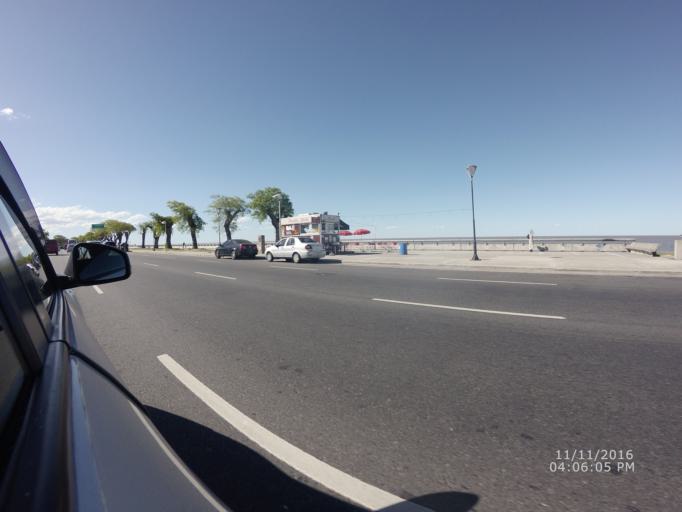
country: AR
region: Buenos Aires F.D.
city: Retiro
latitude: -34.5621
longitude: -58.4060
